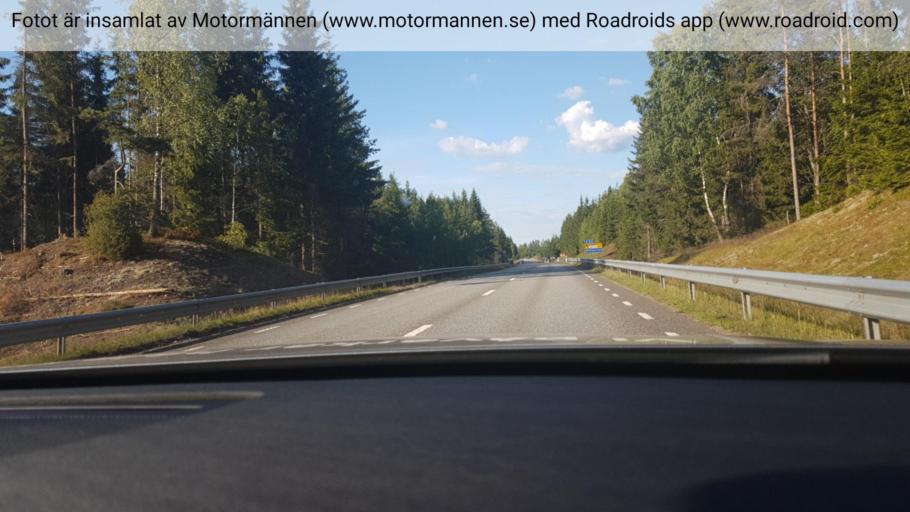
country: SE
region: Joenkoeping
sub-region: Gnosjo Kommun
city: Marieholm
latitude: 57.6106
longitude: 13.7603
